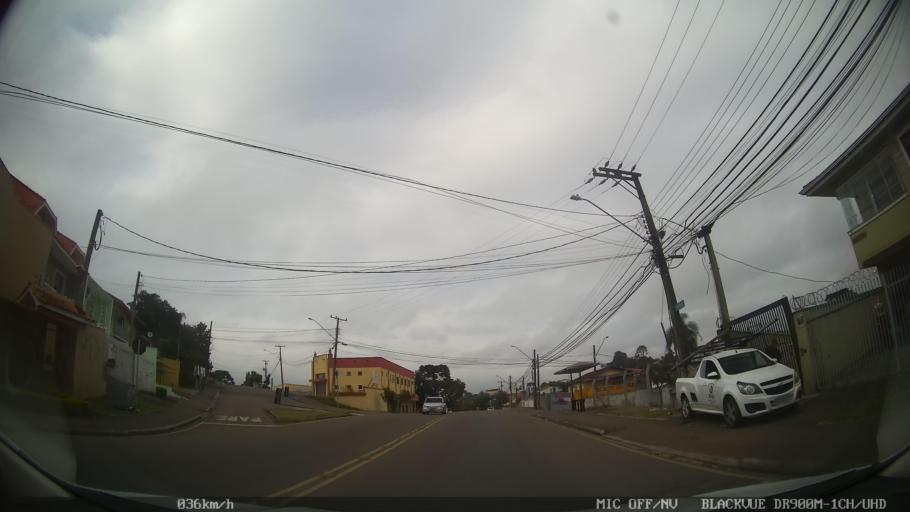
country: BR
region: Parana
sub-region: Almirante Tamandare
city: Almirante Tamandare
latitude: -25.3830
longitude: -49.3346
